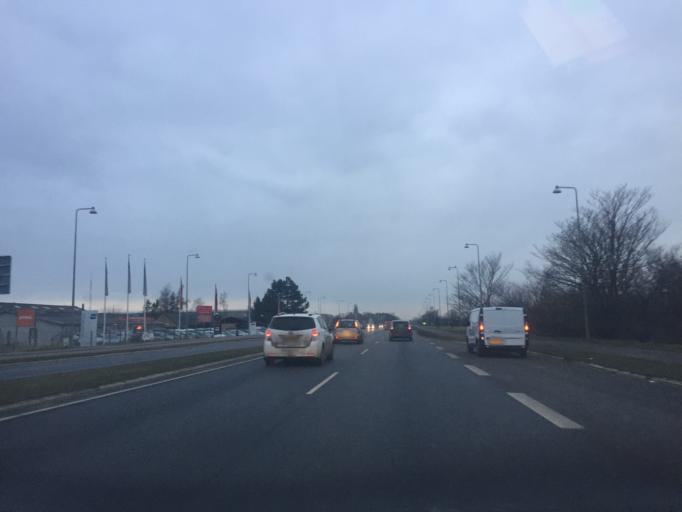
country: DK
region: Zealand
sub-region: Solrod Kommune
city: Solrod
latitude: 55.5004
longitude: 12.1967
